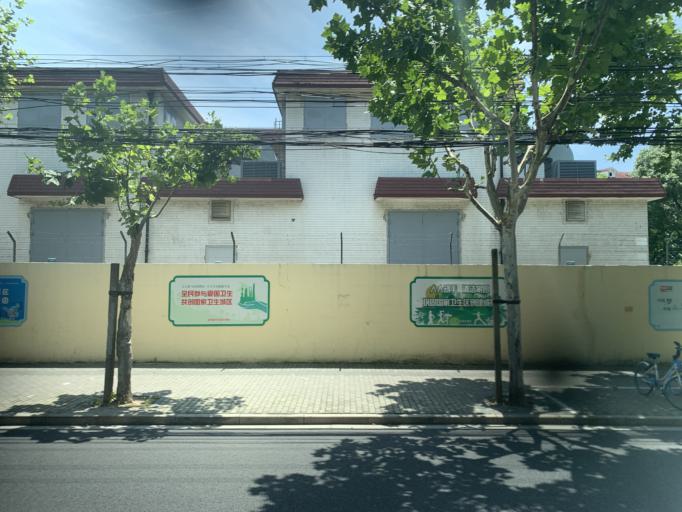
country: CN
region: Shanghai Shi
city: Pudong
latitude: 31.2493
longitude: 121.5713
